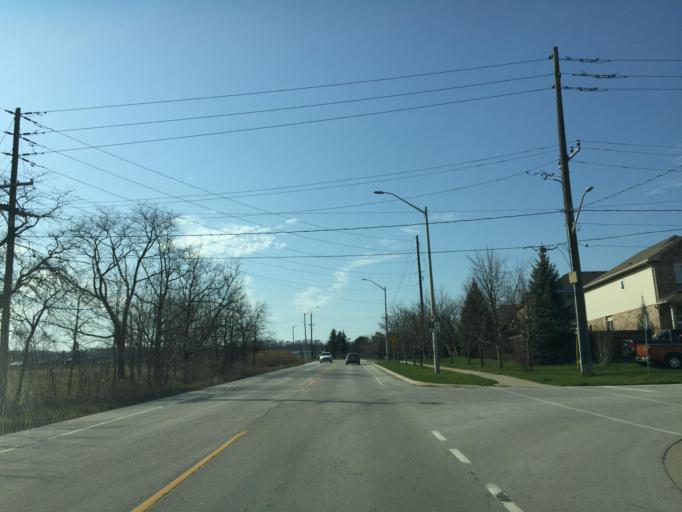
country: CA
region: Ontario
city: Hamilton
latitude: 43.2976
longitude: -79.8947
